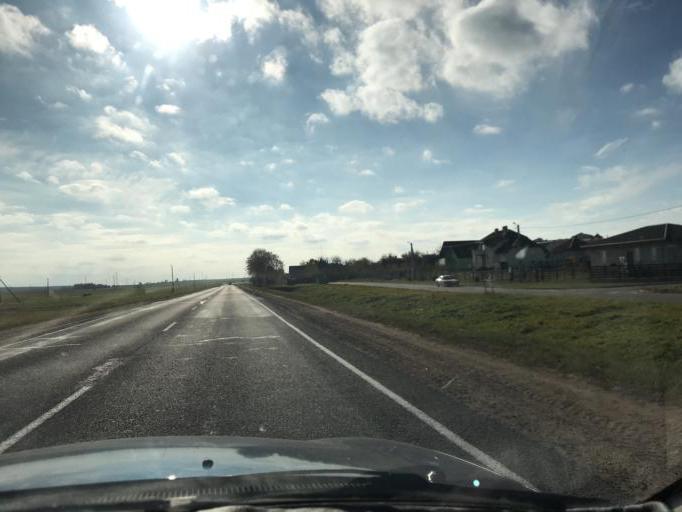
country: BY
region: Grodnenskaya
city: Voranava
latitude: 54.1552
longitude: 25.3257
